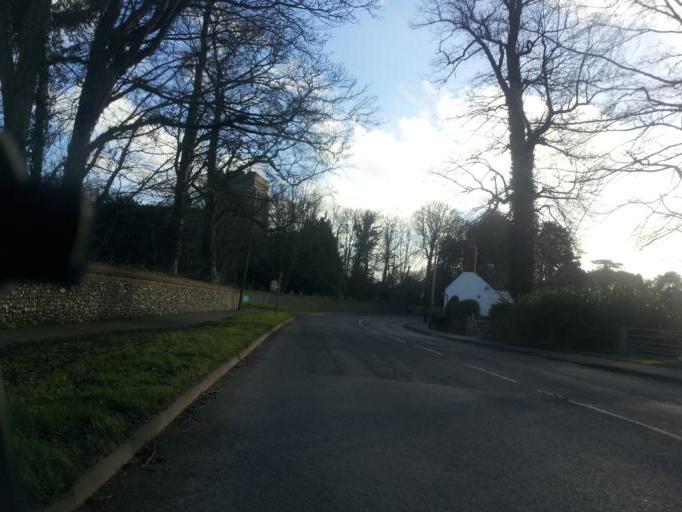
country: GB
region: England
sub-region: Kent
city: Meopham
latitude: 51.3723
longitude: 0.3605
